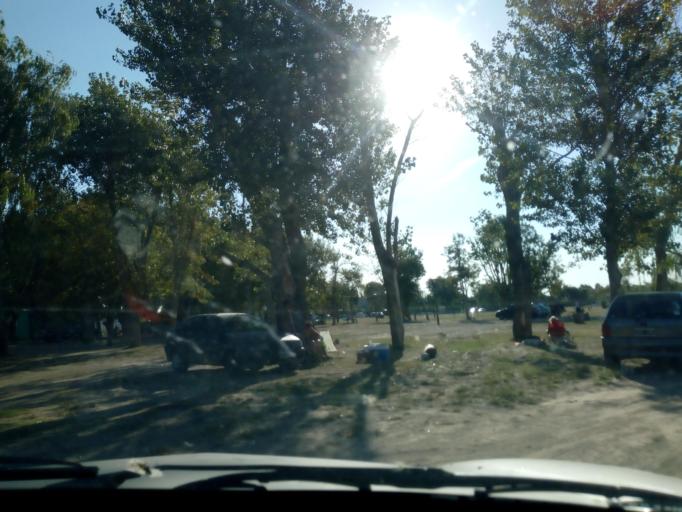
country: AR
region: Buenos Aires
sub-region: Partido de Ensenada
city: Ensenada
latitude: -34.8260
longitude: -57.9583
